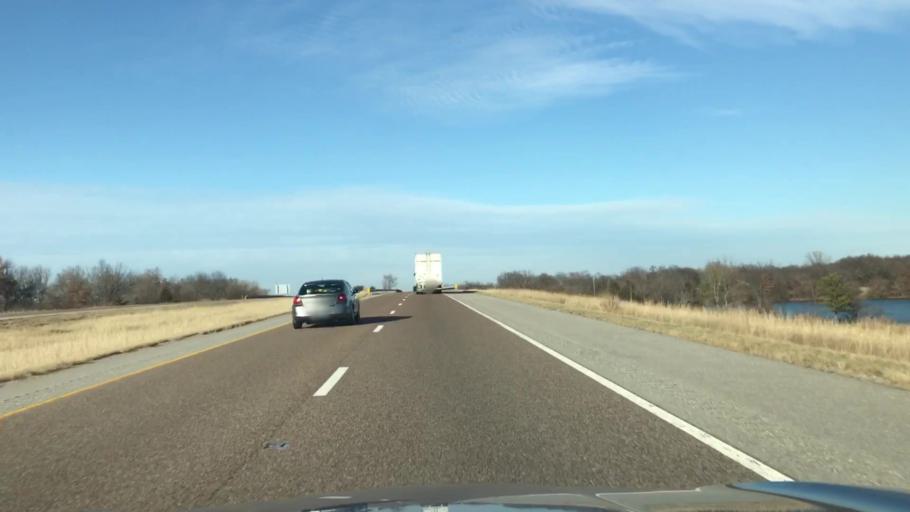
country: US
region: Illinois
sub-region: Macoupin County
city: Staunton
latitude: 38.9766
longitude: -89.7491
